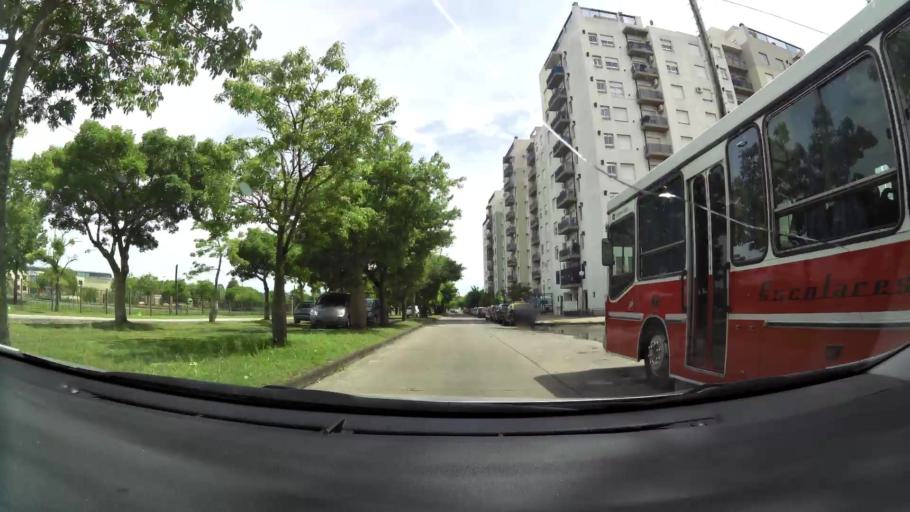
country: AR
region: Buenos Aires F.D.
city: Villa Lugano
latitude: -34.6626
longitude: -58.4671
